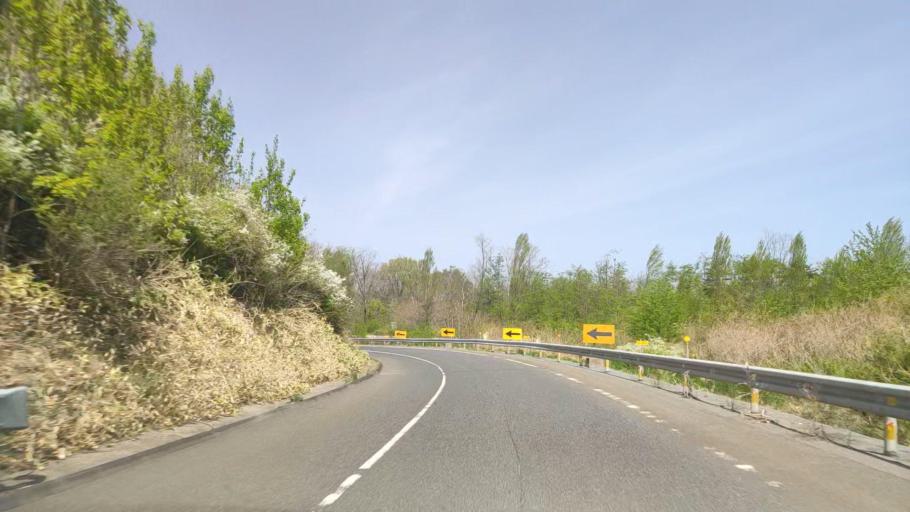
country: JP
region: Aomori
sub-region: Hachinohe Shi
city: Uchimaru
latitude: 40.4938
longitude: 141.4645
